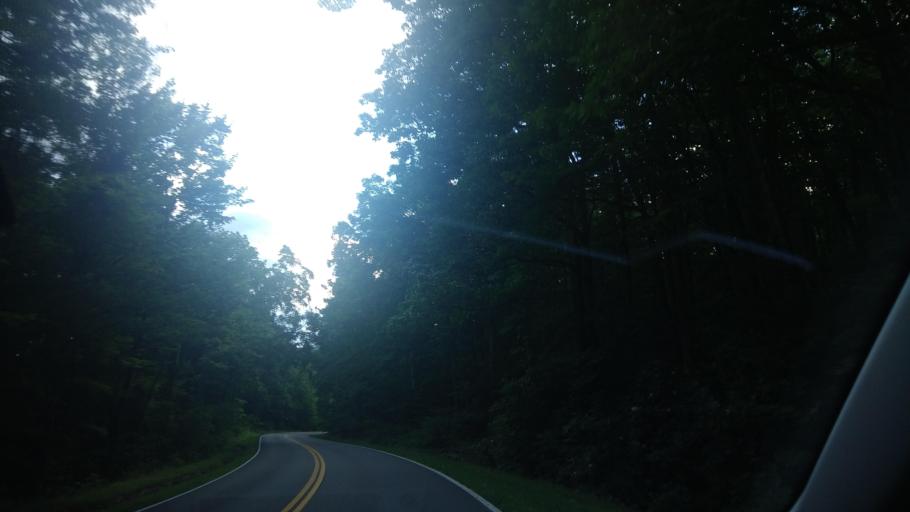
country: US
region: Tennessee
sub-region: Cocke County
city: Newport
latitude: 35.8279
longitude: -83.1998
